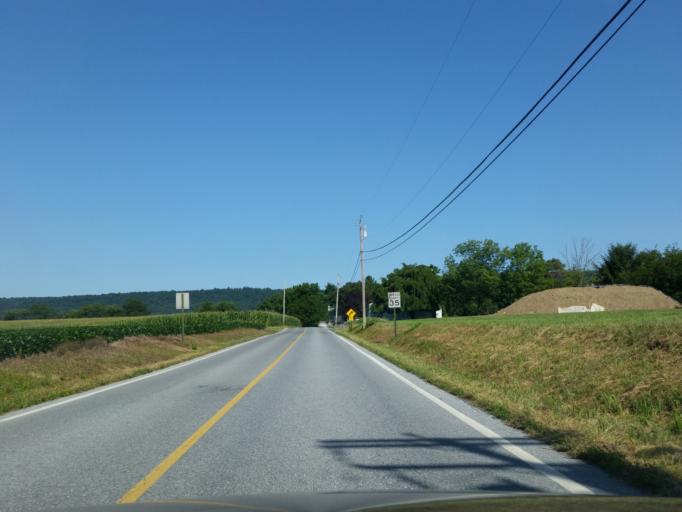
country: US
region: Pennsylvania
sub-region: Lebanon County
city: Jonestown
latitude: 40.4473
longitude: -76.5325
